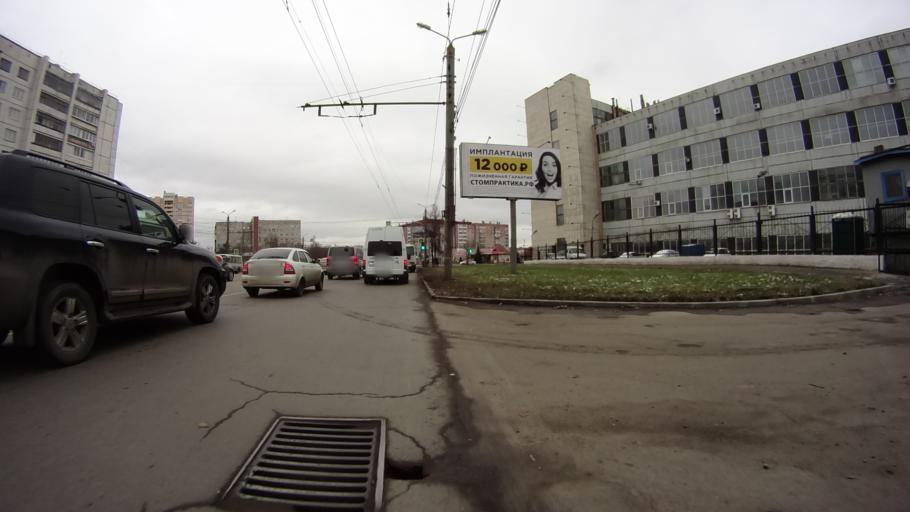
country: RU
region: Chelyabinsk
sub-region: Gorod Chelyabinsk
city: Chelyabinsk
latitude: 55.1928
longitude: 61.3598
